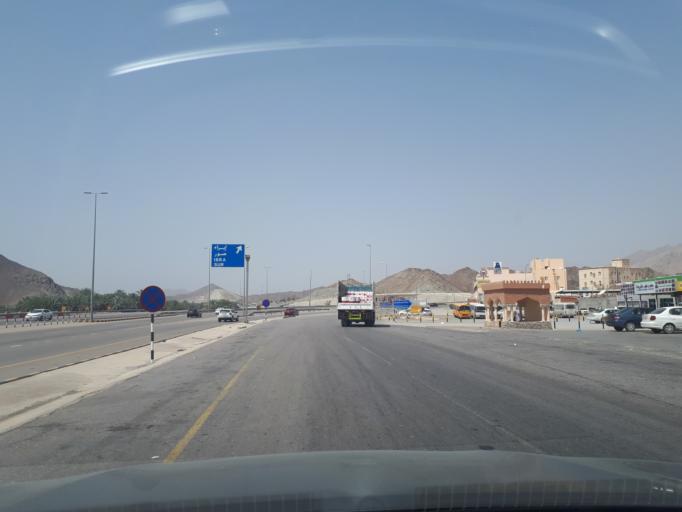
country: OM
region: Muhafazat ad Dakhiliyah
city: Bidbid
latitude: 23.4153
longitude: 58.1060
